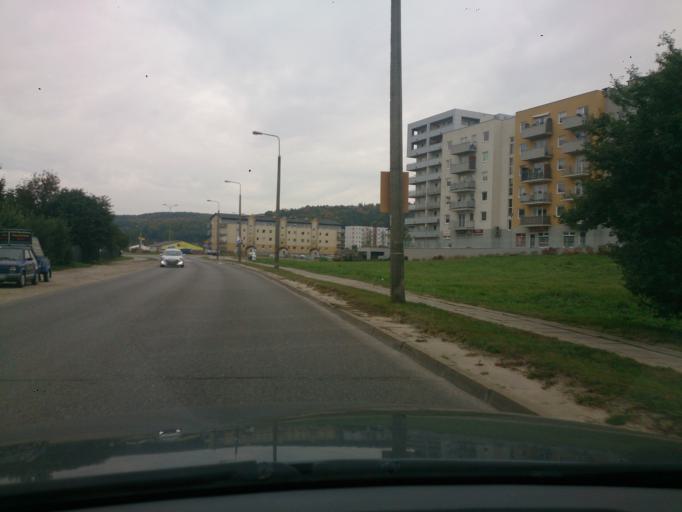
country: PL
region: Pomeranian Voivodeship
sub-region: Powiat wejherowski
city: Reda
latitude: 54.5958
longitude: 18.3619
